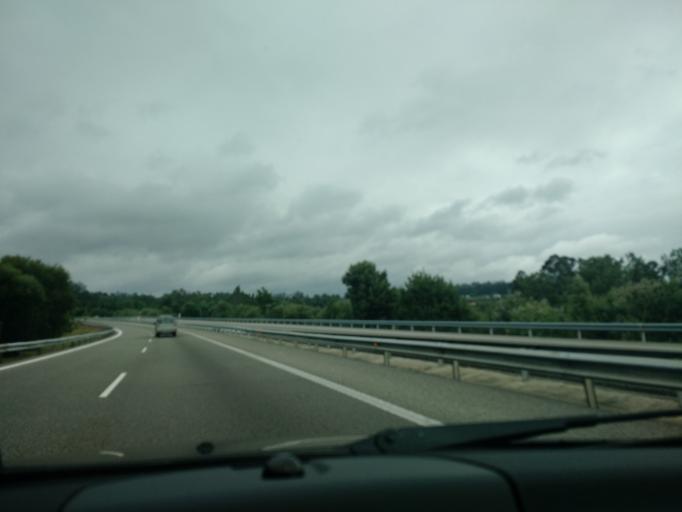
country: ES
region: Galicia
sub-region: Provincia da Coruna
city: Bergondo
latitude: 43.2857
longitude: -8.2766
